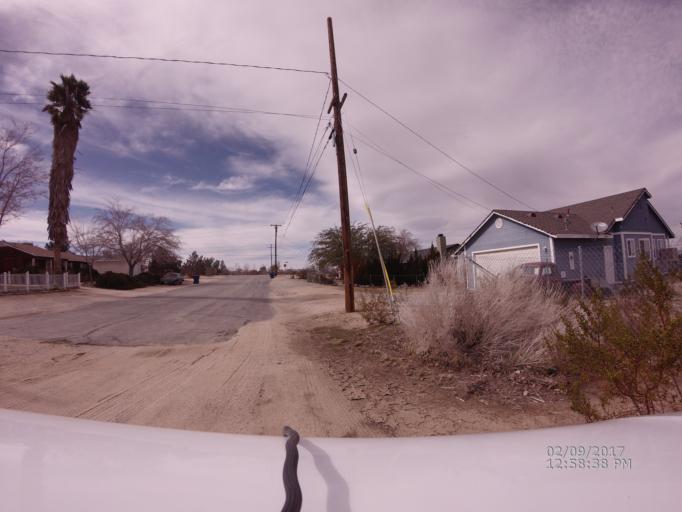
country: US
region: California
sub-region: Los Angeles County
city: Littlerock
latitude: 34.5036
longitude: -117.8956
